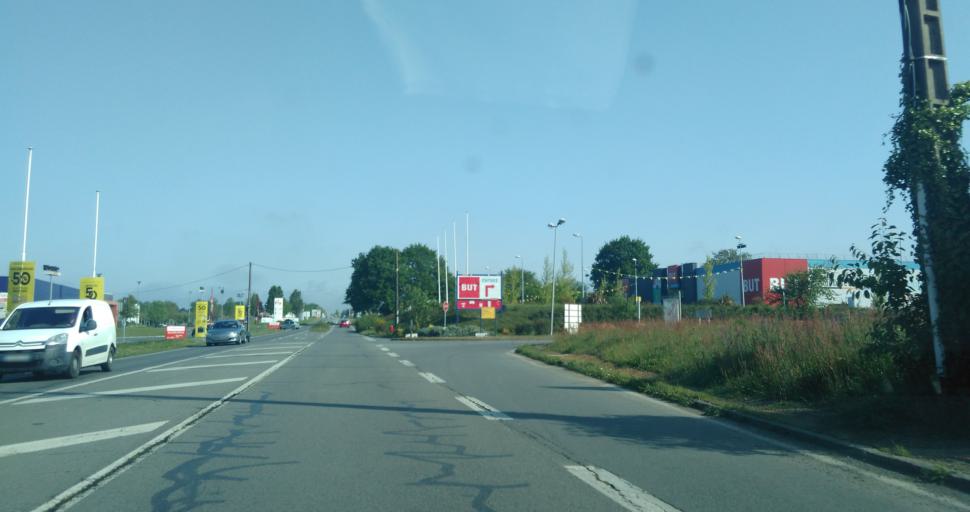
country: FR
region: Brittany
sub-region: Departement d'Ille-et-Vilaine
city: La Chapelle-des-Fougeretz
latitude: 48.1887
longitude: -1.7273
